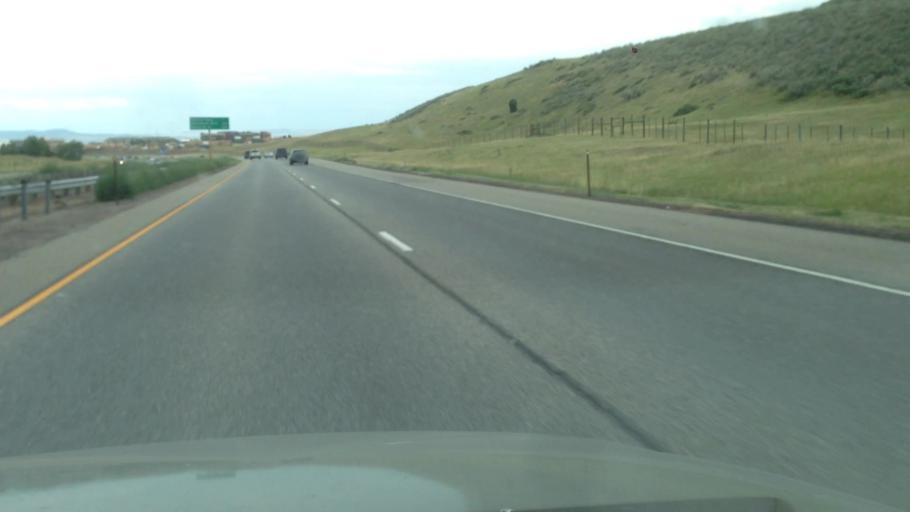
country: US
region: Colorado
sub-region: Jefferson County
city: Ken Caryl
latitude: 39.5665
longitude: -105.1307
